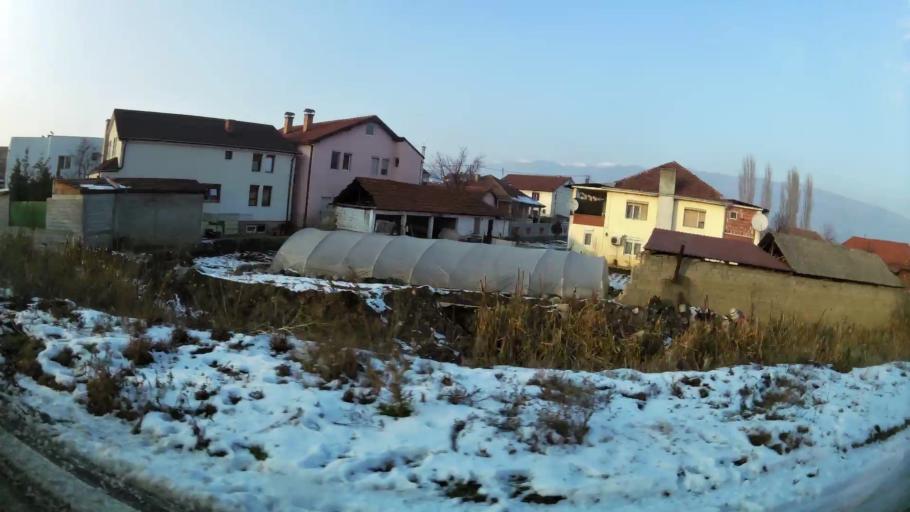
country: MK
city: Creshevo
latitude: 42.0166
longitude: 21.5144
